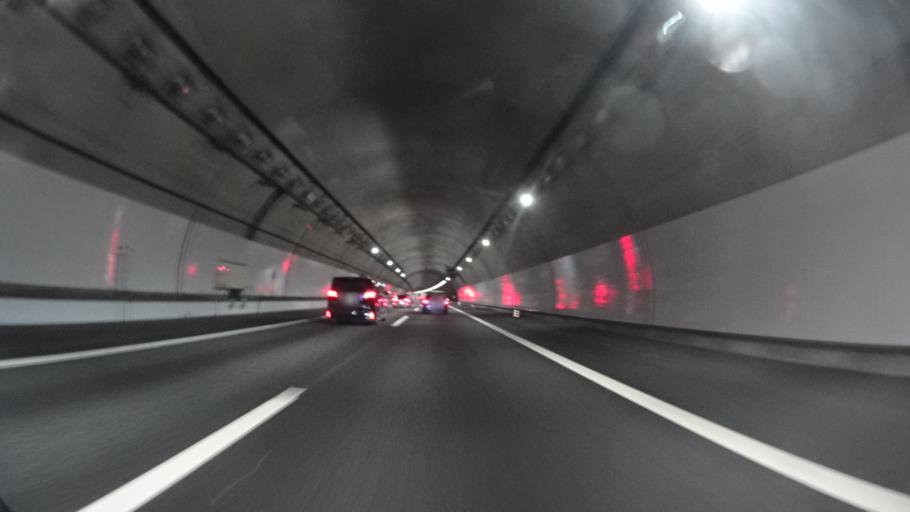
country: JP
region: Shiga Prefecture
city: Minakuchicho-matoba
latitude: 34.9208
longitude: 136.1345
